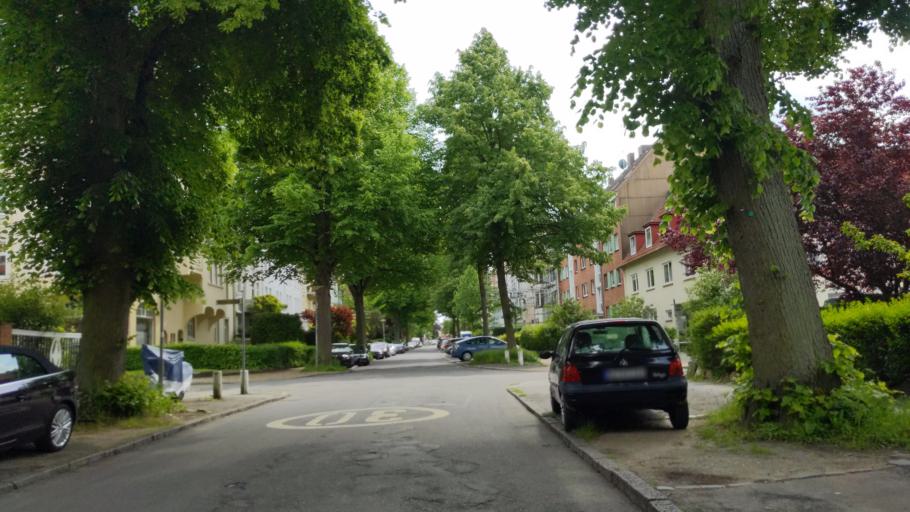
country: DE
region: Schleswig-Holstein
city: Luebeck
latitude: 53.8578
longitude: 10.6978
